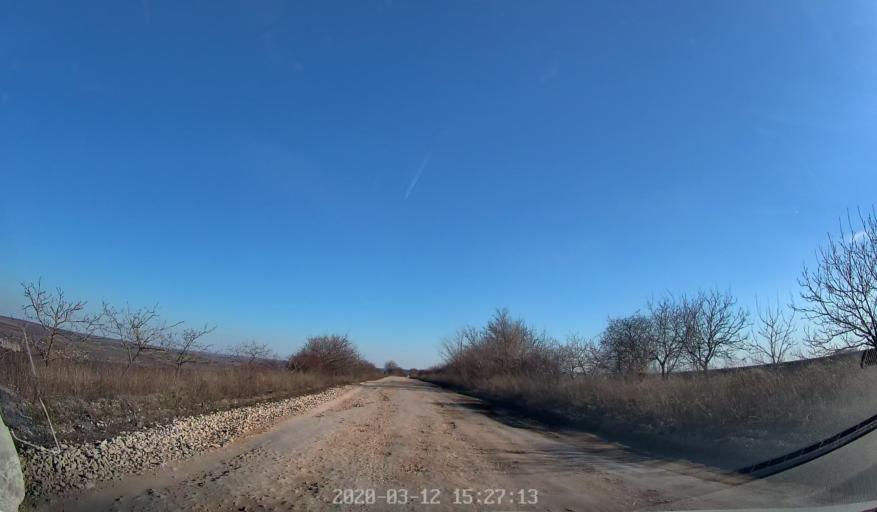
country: MD
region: Chisinau
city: Ciorescu
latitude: 47.1740
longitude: 28.9255
